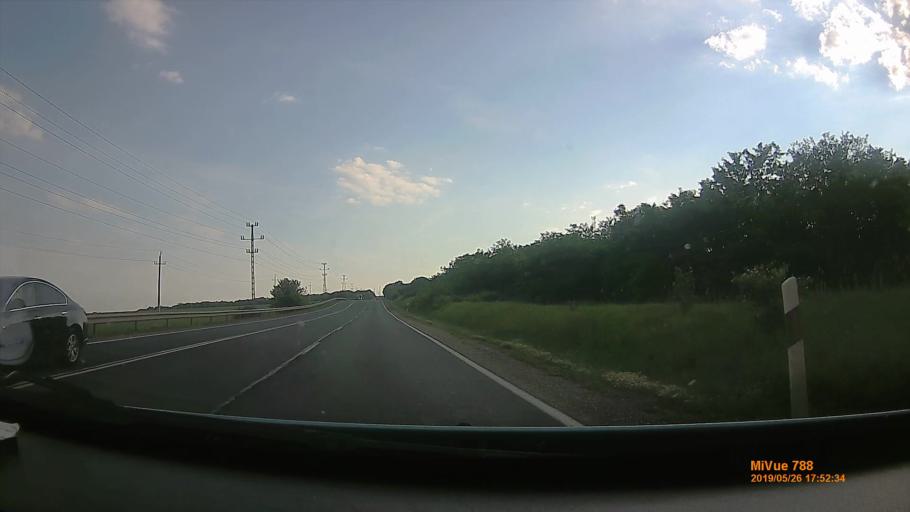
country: HU
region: Borsod-Abauj-Zemplen
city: Szikszo
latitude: 48.1632
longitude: 20.9054
